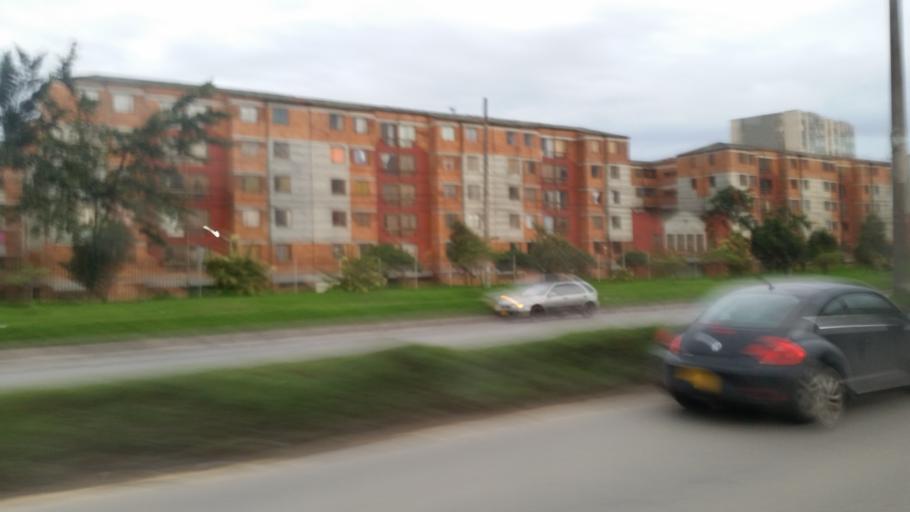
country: CO
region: Cundinamarca
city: Funza
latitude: 4.6724
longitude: -74.1525
